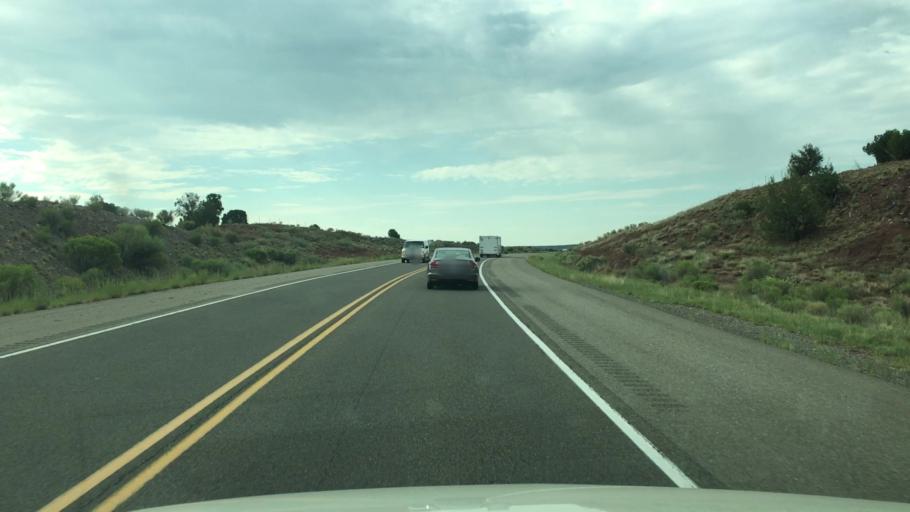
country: US
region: New Mexico
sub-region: Santa Fe County
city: Eldorado at Santa Fe
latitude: 35.2700
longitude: -105.8098
